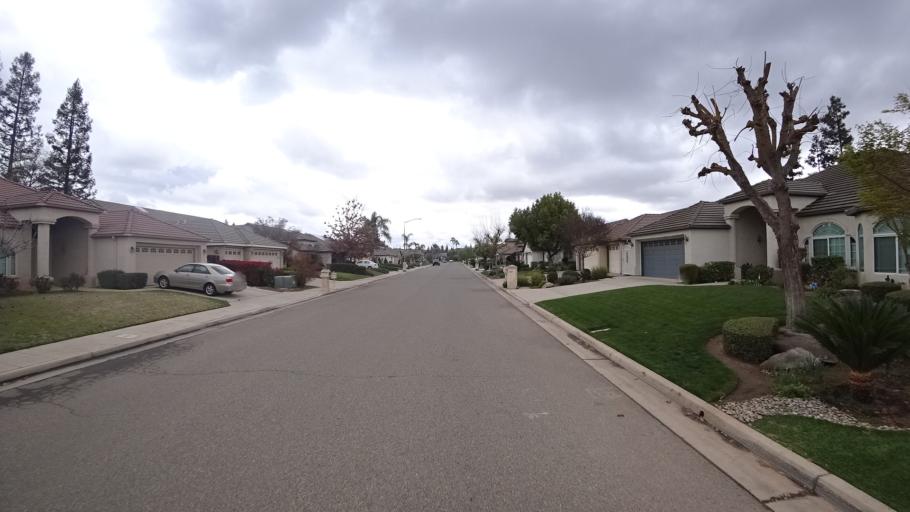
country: US
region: California
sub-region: Fresno County
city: Fresno
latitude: 36.8382
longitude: -119.8323
